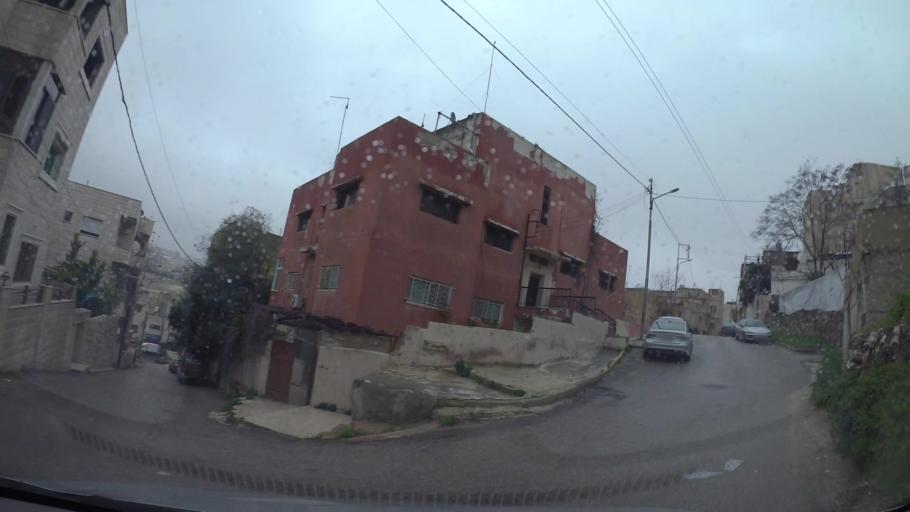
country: JO
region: Amman
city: Al Jubayhah
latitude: 32.0266
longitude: 35.8379
